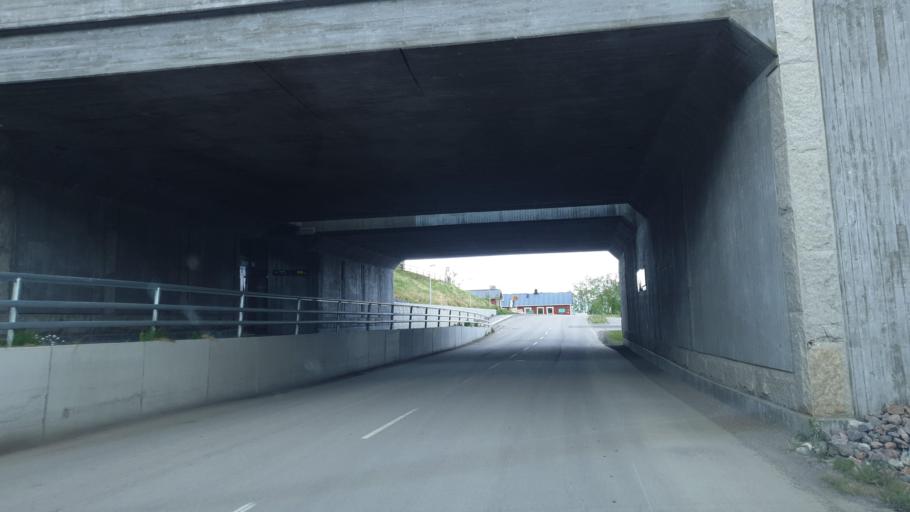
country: NO
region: Troms
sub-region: Bardu
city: Setermoen
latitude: 68.3487
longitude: 18.8290
